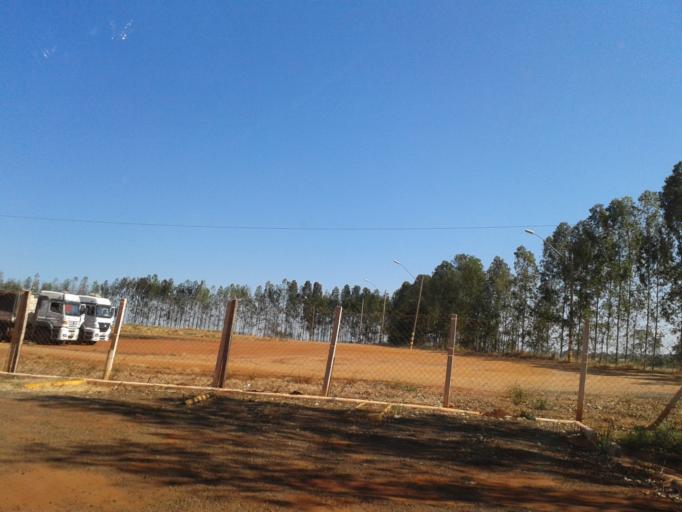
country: BR
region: Minas Gerais
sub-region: Capinopolis
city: Capinopolis
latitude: -18.7397
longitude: -49.5510
